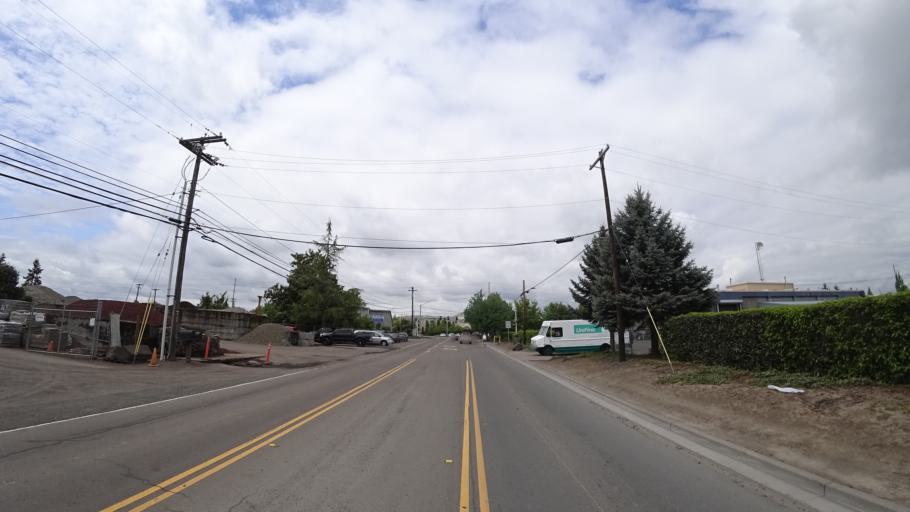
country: US
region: Oregon
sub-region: Washington County
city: Rockcreek
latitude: 45.5377
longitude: -122.8986
